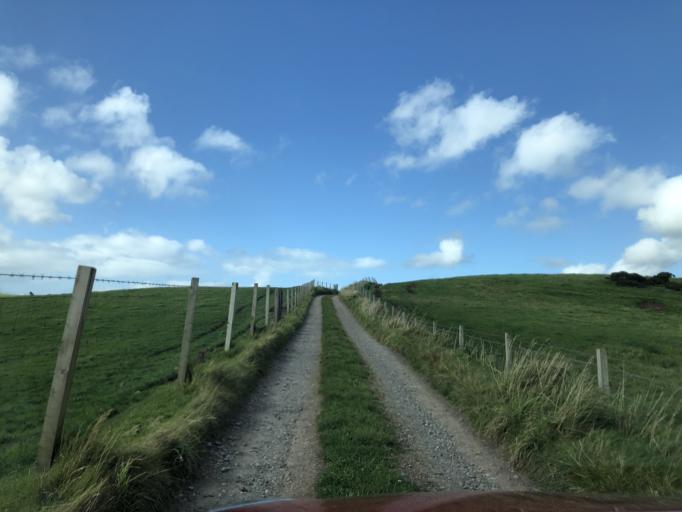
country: GB
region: Scotland
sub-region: Argyll and Bute
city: Campbeltown
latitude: 55.3124
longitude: -5.6077
